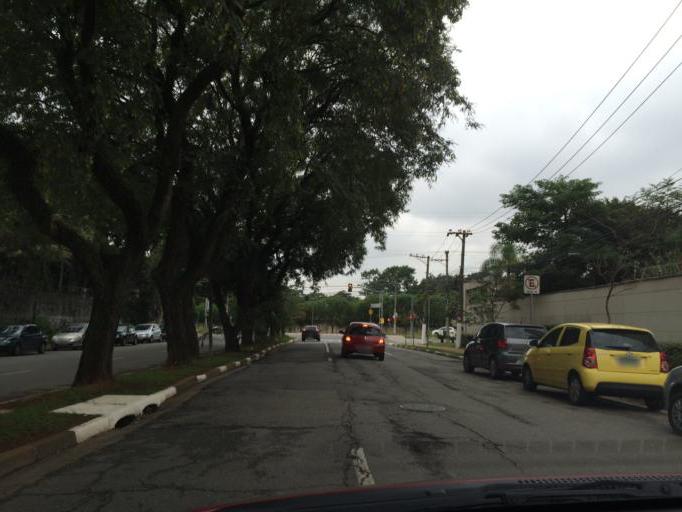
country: BR
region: Sao Paulo
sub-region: Osasco
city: Osasco
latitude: -23.5543
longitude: -46.7367
